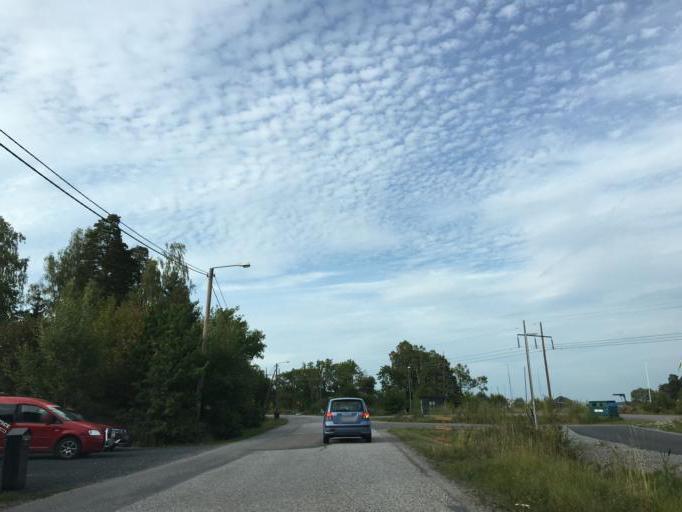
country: SE
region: Soedermanland
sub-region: Eskilstuna Kommun
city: Torshalla
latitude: 59.4513
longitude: 16.4669
